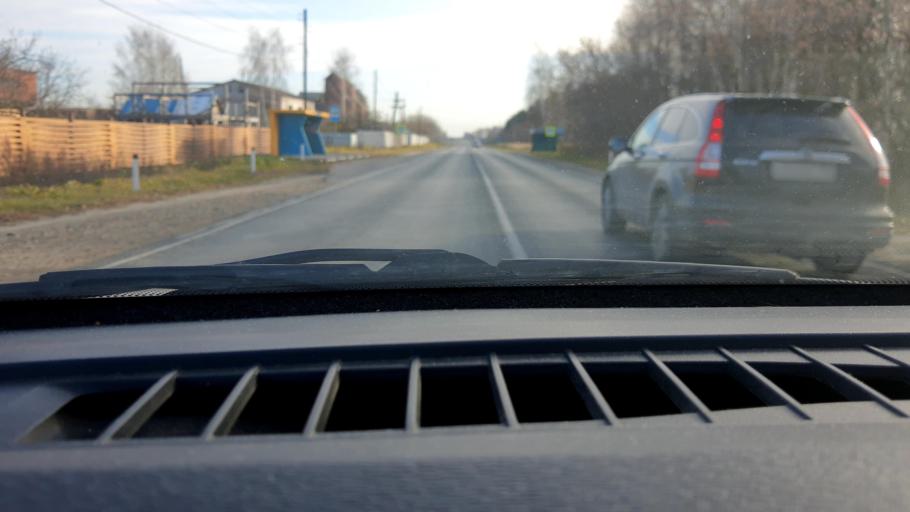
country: RU
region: Nizjnij Novgorod
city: Gorodets
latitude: 56.6368
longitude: 43.5259
